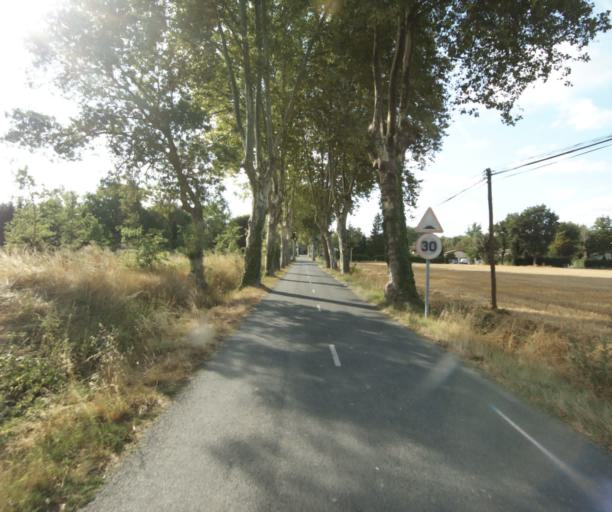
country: FR
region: Midi-Pyrenees
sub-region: Departement de la Haute-Garonne
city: Revel
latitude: 43.4928
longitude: 1.9726
